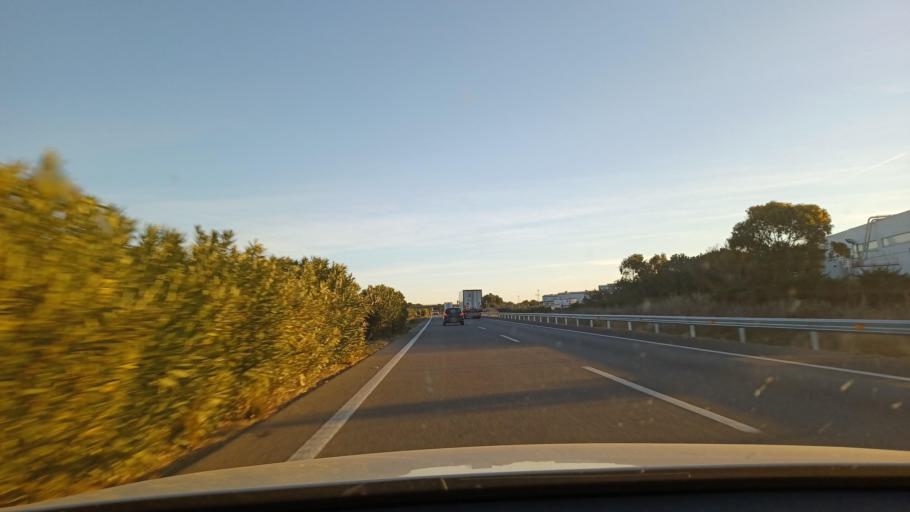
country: ES
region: Catalonia
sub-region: Provincia de Tarragona
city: Cambrils
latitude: 41.0940
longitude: 1.0901
